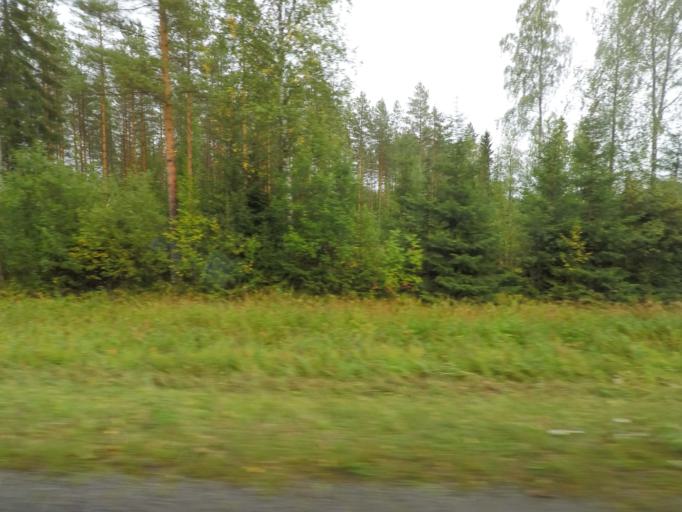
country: FI
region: Southern Savonia
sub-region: Pieksaemaeki
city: Joroinen
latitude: 62.0713
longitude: 27.8158
